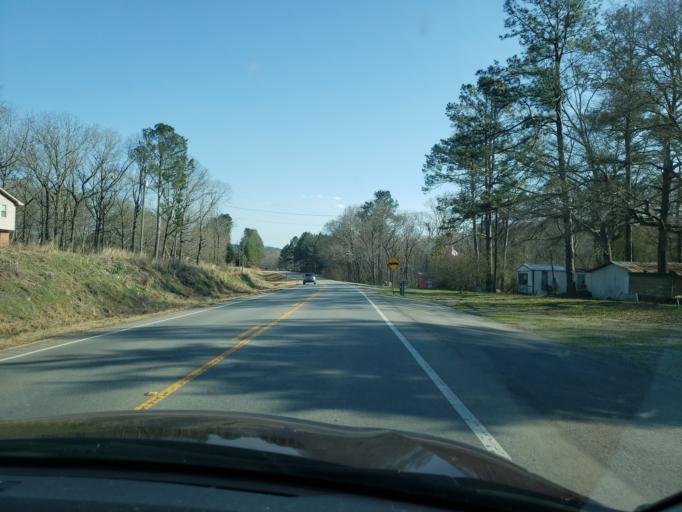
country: US
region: Alabama
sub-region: Cleburne County
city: Heflin
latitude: 33.5186
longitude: -85.6343
